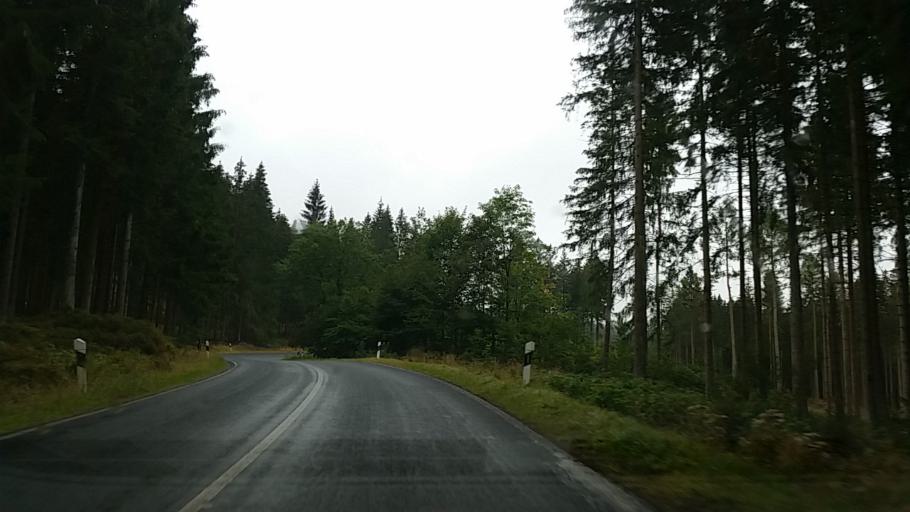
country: DE
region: Lower Saxony
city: Altenau
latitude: 51.7860
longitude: 10.4341
